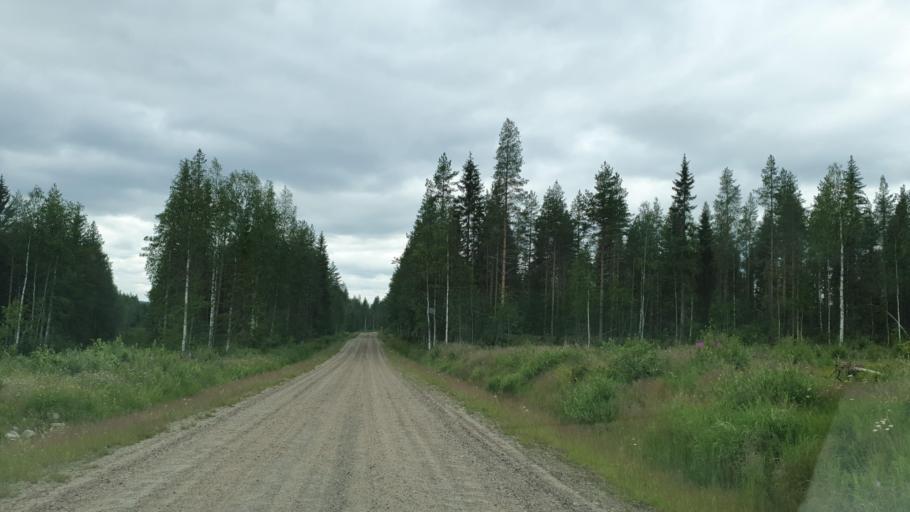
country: FI
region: Kainuu
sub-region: Kehys-Kainuu
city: Kuhmo
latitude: 64.0109
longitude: 29.3464
